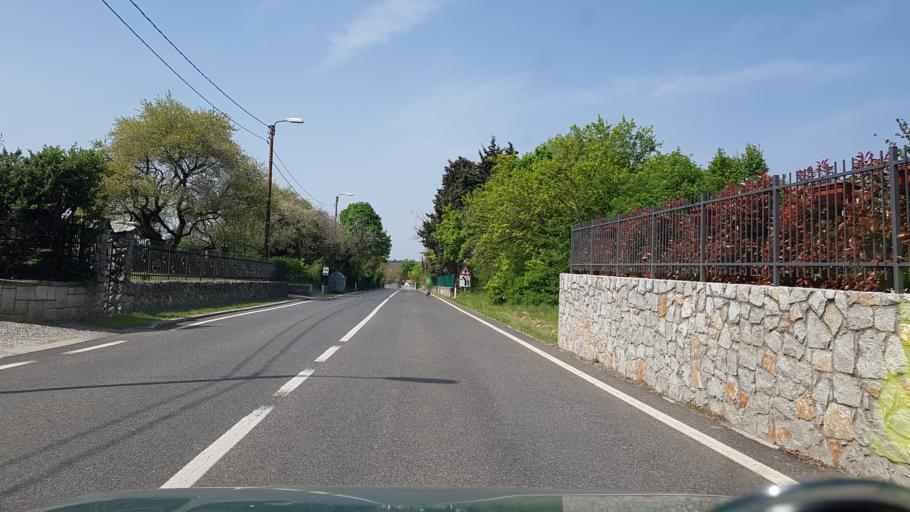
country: IT
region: Friuli Venezia Giulia
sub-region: Provincia di Trieste
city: Dolina
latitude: 45.6404
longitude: 13.8617
